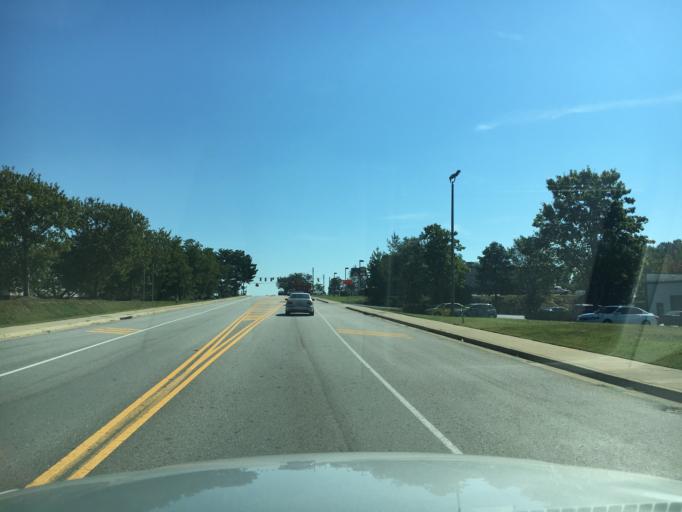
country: US
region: South Carolina
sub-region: Greenville County
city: Five Forks
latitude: 34.8367
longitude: -82.2831
